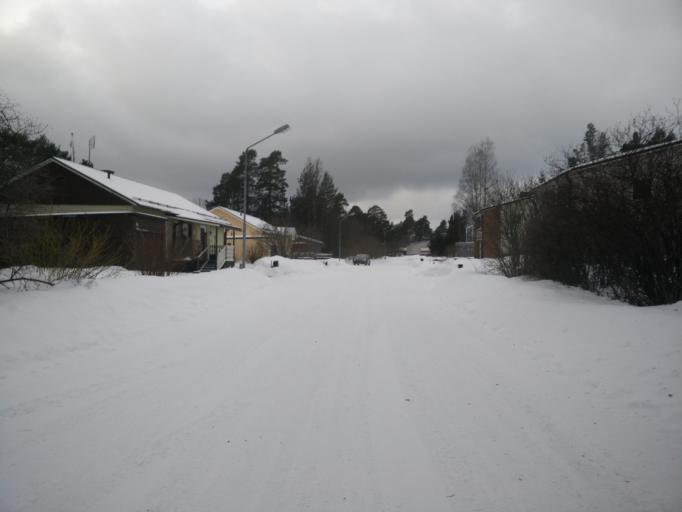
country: SE
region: Vaesternorrland
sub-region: Sundsvalls Kommun
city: Nolby
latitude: 62.2868
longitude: 17.3650
